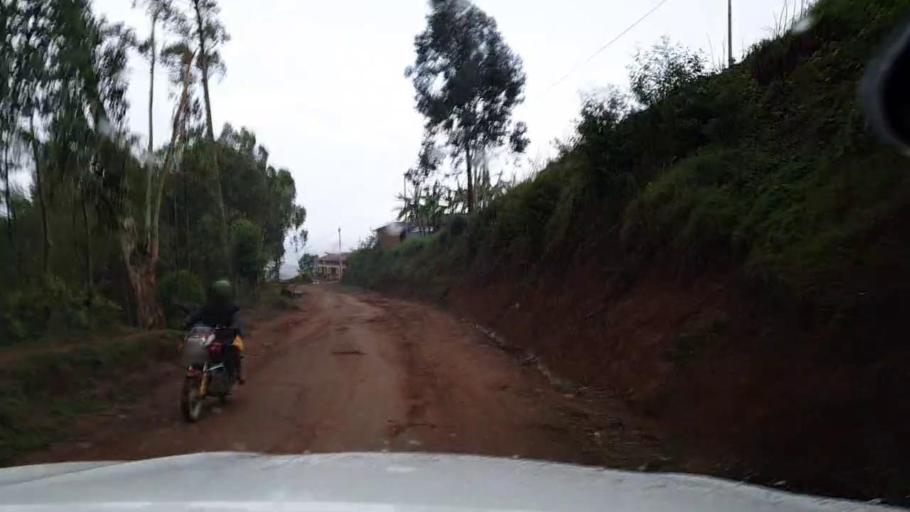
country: BI
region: Kayanza
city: Kayanza
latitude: -2.7818
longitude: 29.5345
